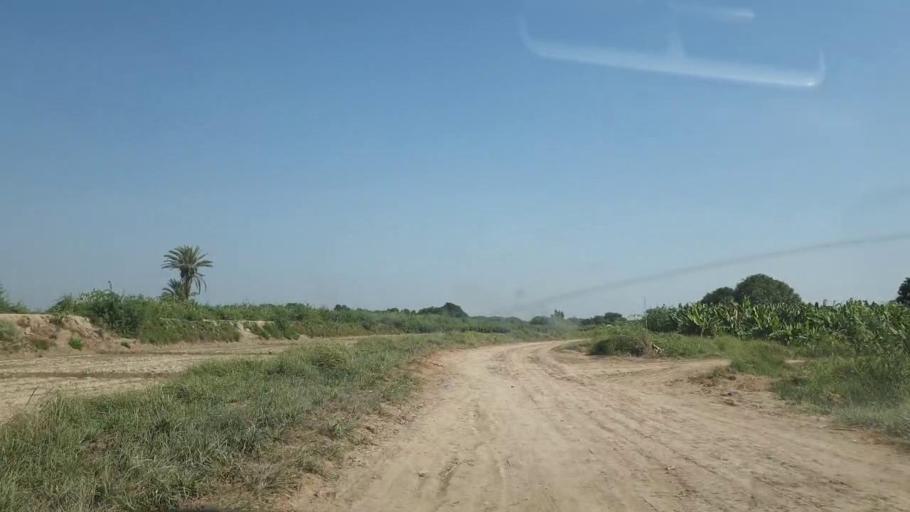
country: PK
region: Sindh
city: Tando Jam
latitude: 25.3700
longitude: 68.5808
